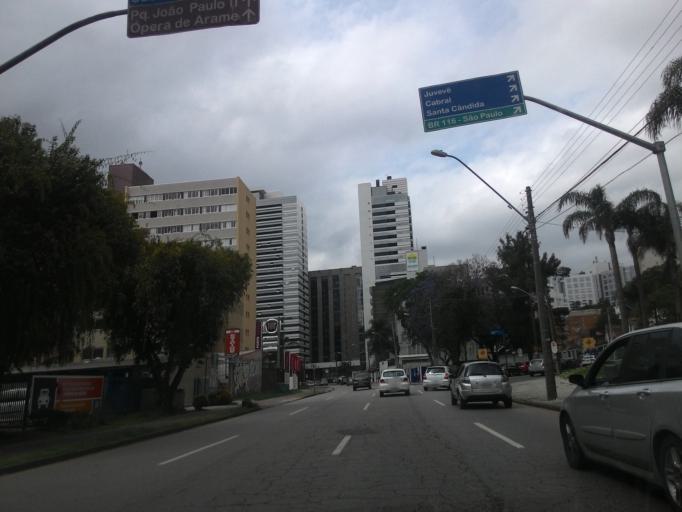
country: BR
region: Parana
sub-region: Curitiba
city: Curitiba
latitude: -25.4225
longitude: -49.2685
